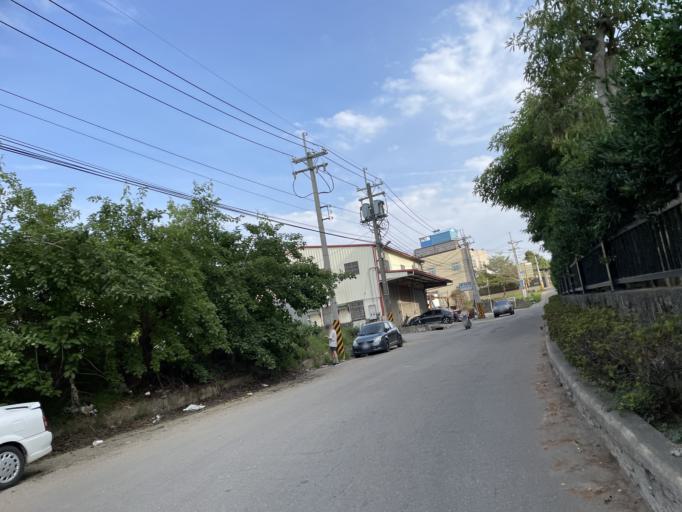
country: TW
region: Taiwan
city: Fengyuan
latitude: 24.2172
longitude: 120.7275
